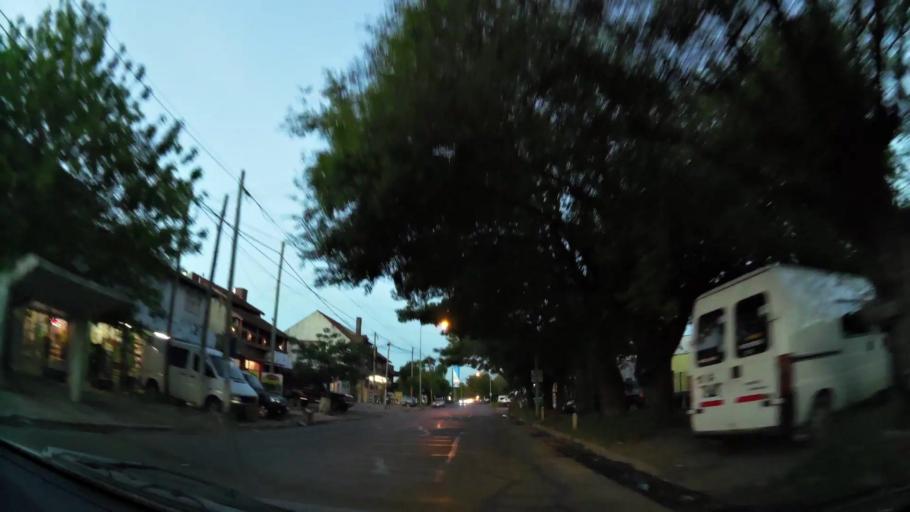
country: AR
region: Buenos Aires
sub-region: Partido de Quilmes
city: Quilmes
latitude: -34.7786
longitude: -58.2235
